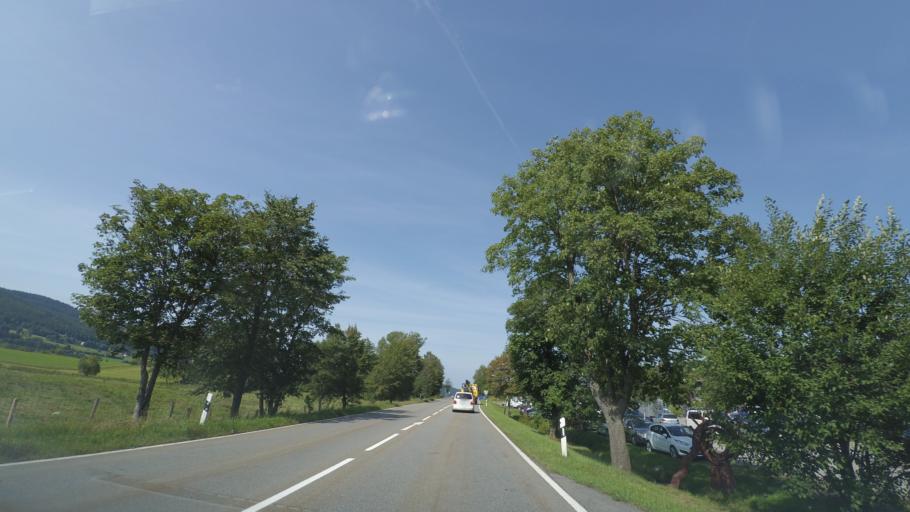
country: DE
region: Bavaria
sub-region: Lower Bavaria
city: Arnbruck
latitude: 49.1274
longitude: 12.9949
